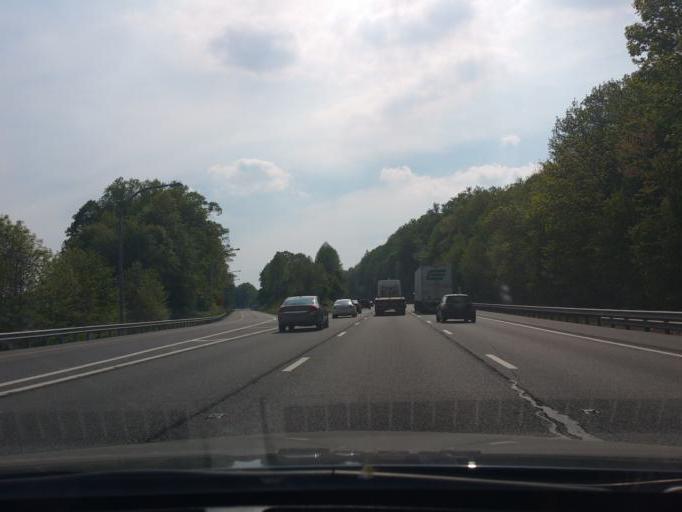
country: US
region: Maryland
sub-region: Harford County
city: Riverside
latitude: 39.5020
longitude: -76.2257
